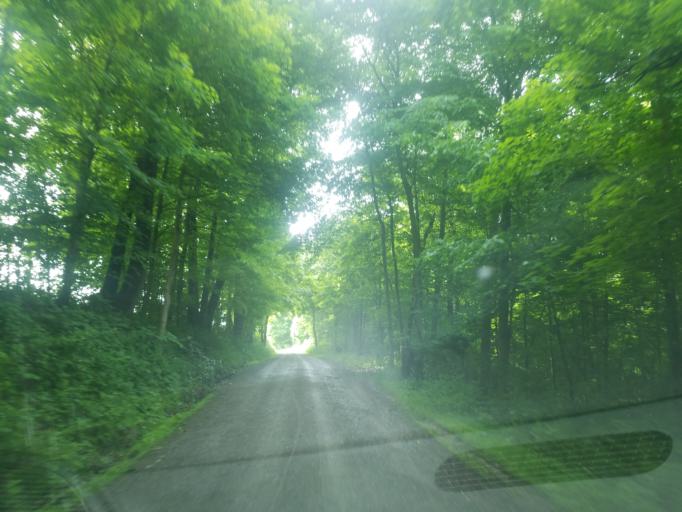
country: US
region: Ohio
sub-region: Holmes County
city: Millersburg
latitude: 40.5156
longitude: -81.8719
